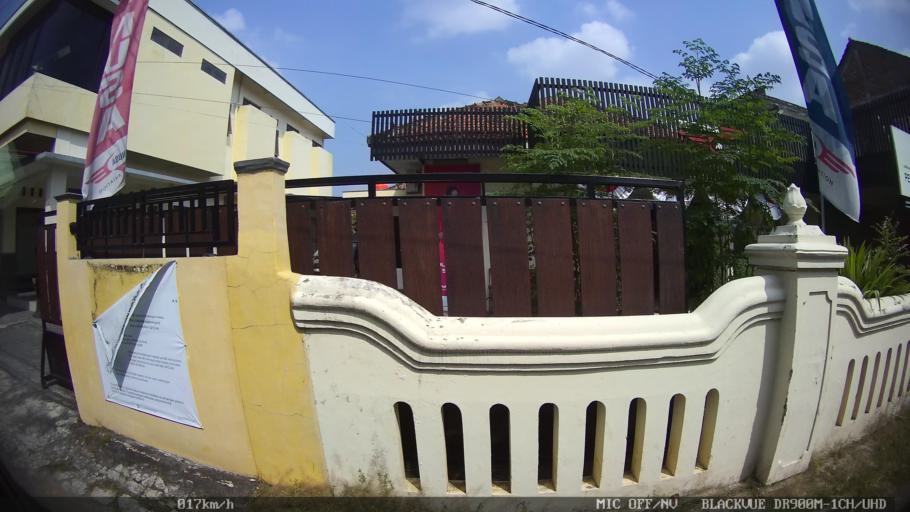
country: ID
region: Daerah Istimewa Yogyakarta
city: Yogyakarta
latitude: -7.8105
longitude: 110.3799
